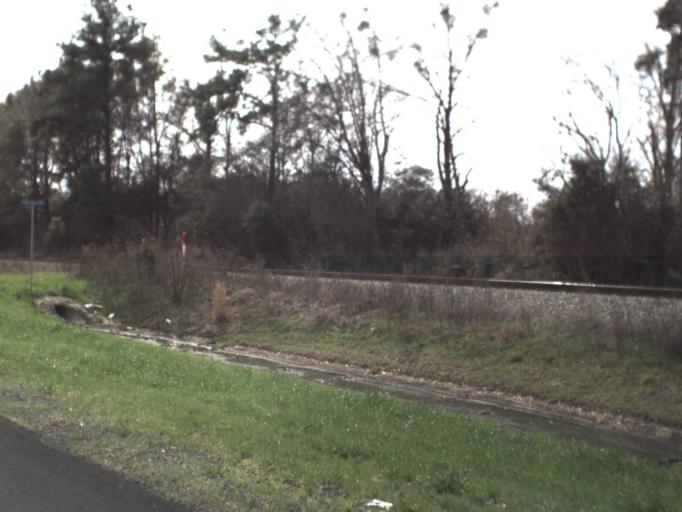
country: US
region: Florida
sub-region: Washington County
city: Chipley
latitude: 30.6864
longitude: -85.3932
